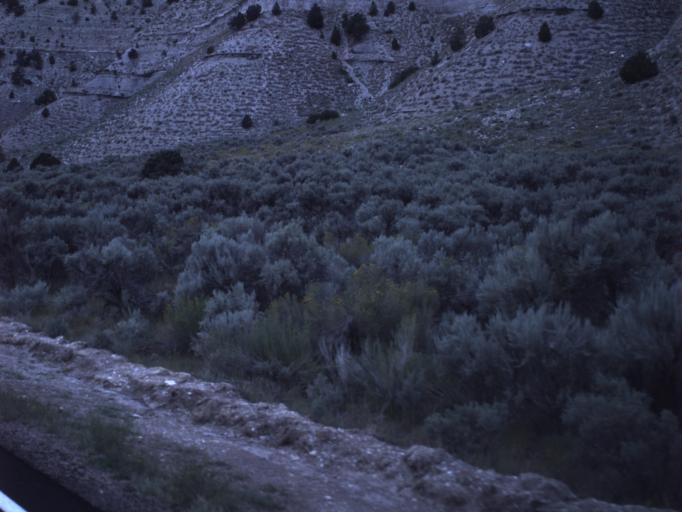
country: US
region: Utah
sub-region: Duchesne County
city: Duchesne
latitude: 39.9717
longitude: -110.6285
